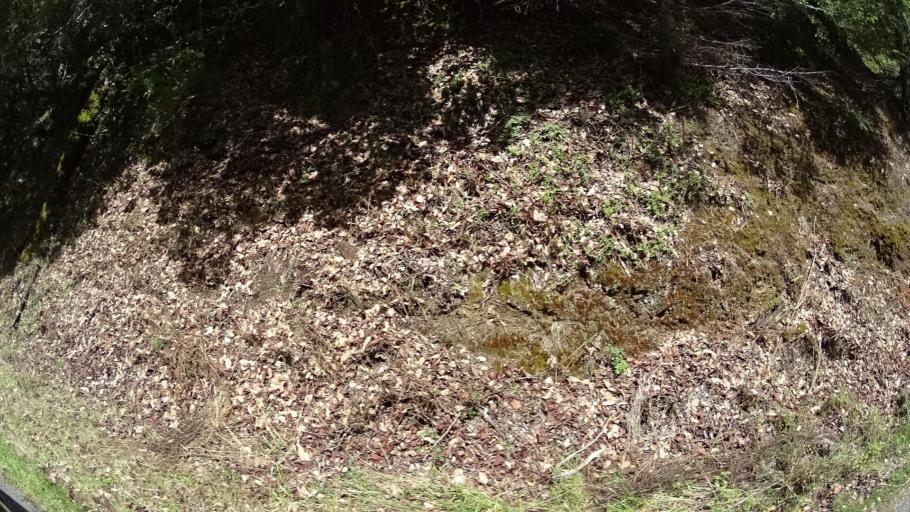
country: US
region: California
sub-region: Humboldt County
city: Blue Lake
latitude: 40.7590
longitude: -123.9169
